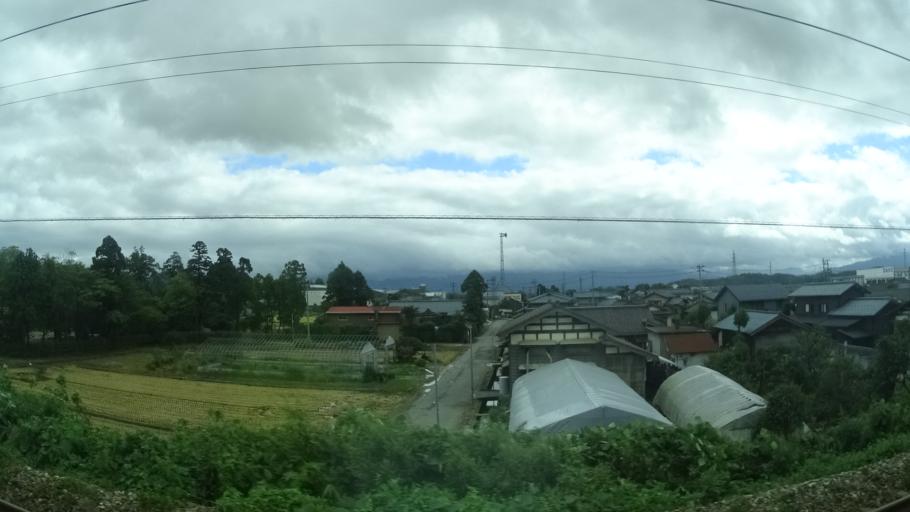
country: JP
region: Niigata
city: Shibata
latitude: 37.9608
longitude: 139.3489
